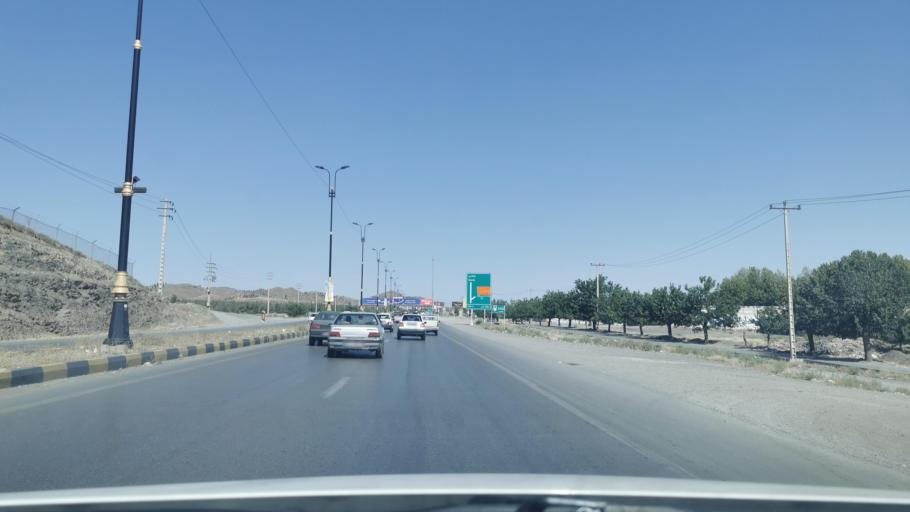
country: IR
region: Razavi Khorasan
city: Torqabeh
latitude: 36.4026
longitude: 59.3856
